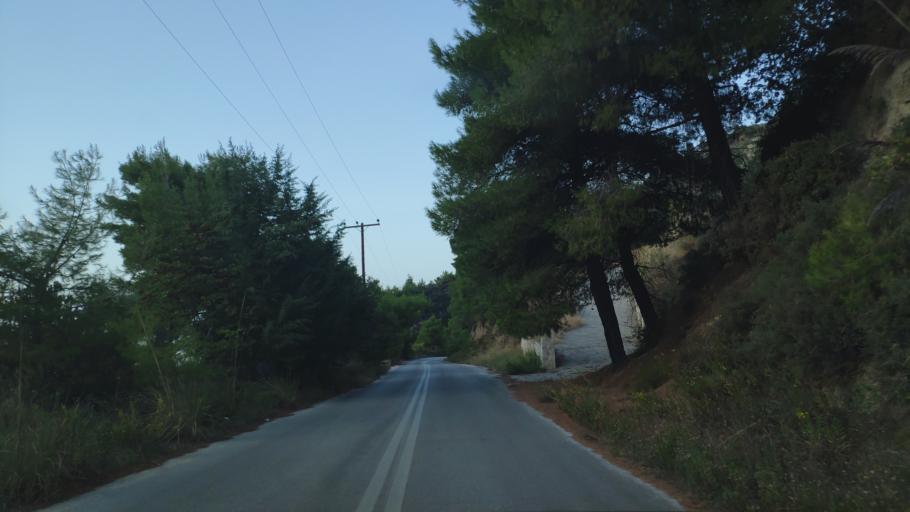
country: GR
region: West Greece
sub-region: Nomos Achaias
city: Aiyira
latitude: 38.0983
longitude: 22.4046
